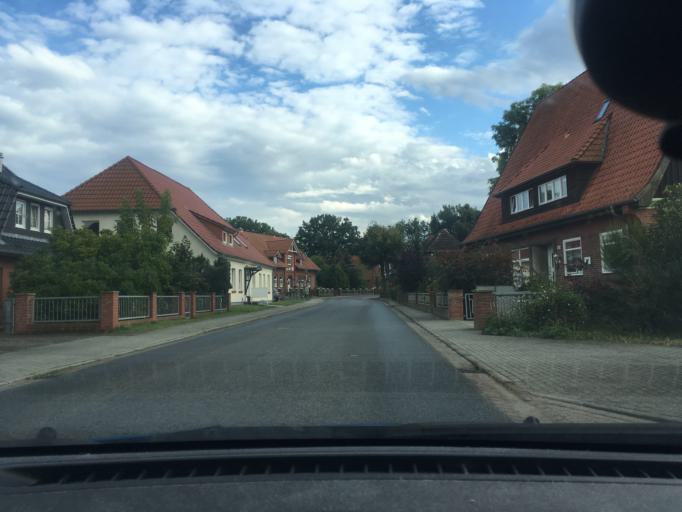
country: DE
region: Lower Saxony
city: Neu Darchau
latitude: 53.2819
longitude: 10.9320
